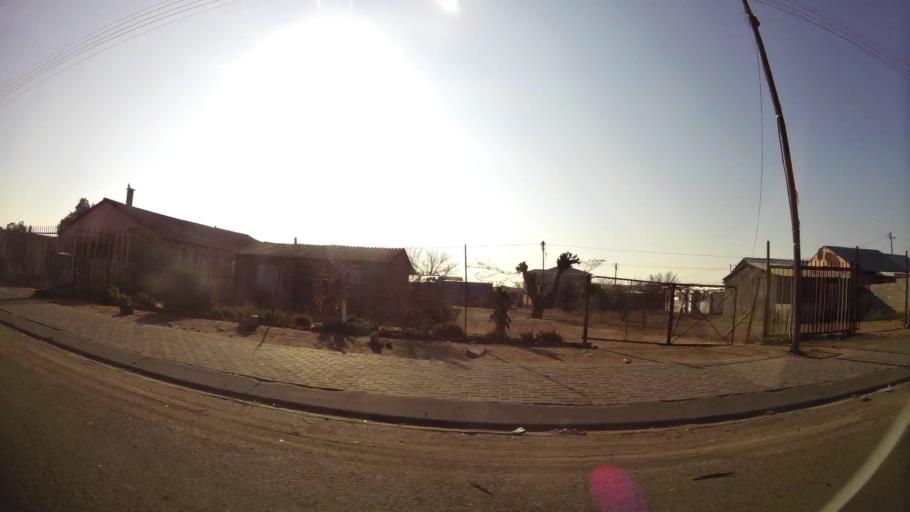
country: ZA
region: Orange Free State
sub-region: Mangaung Metropolitan Municipality
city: Bloemfontein
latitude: -29.1516
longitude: 26.2521
